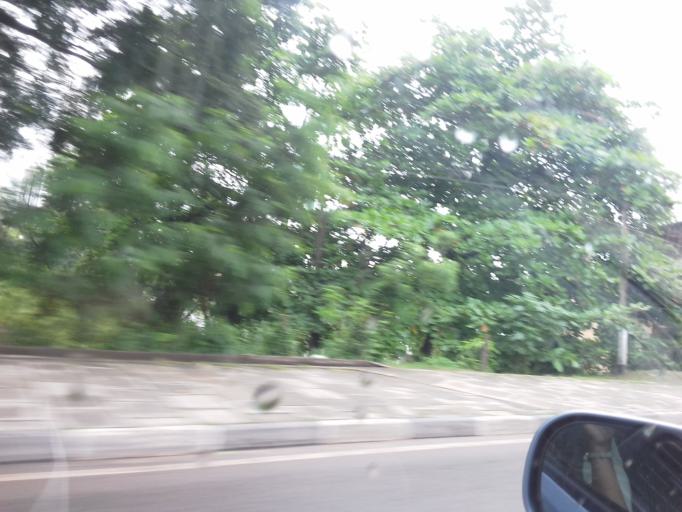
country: LK
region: Western
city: Pita Kotte
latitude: 6.9064
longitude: 79.9031
